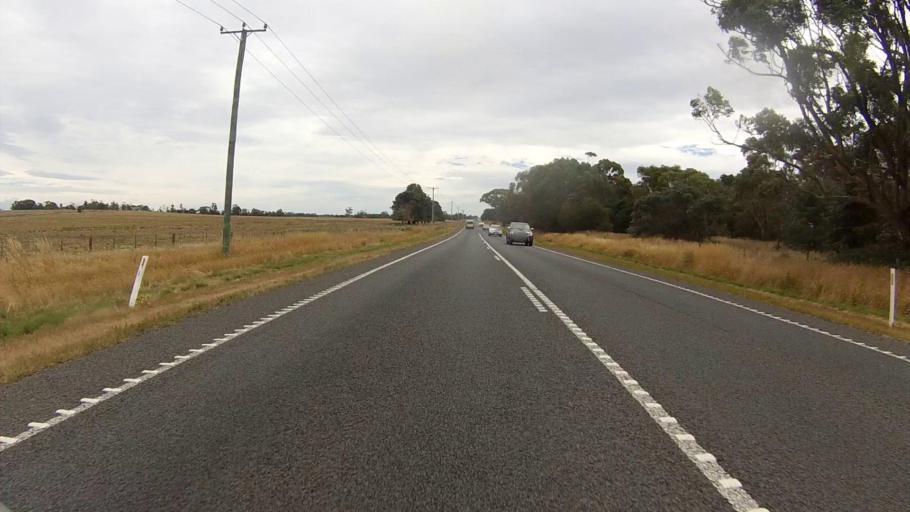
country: AU
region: Tasmania
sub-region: Northern Midlands
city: Evandale
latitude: -41.6975
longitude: 147.2888
